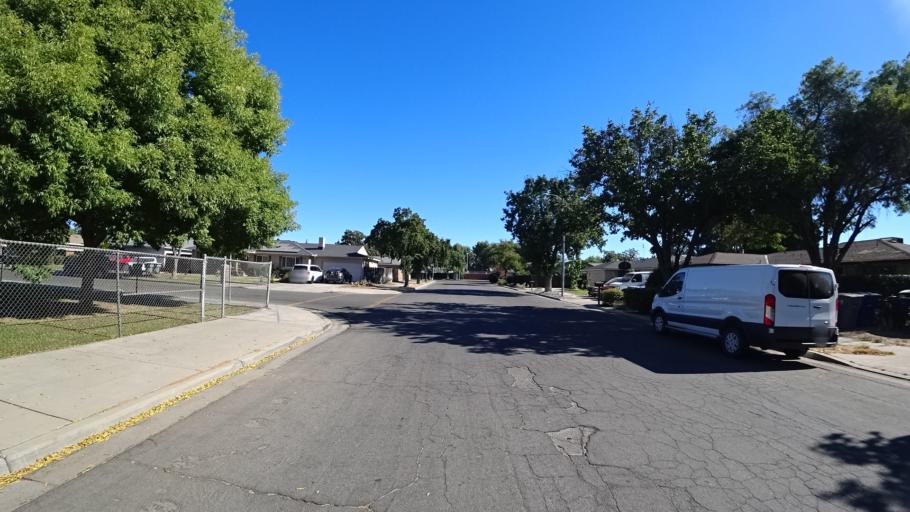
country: US
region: California
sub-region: Fresno County
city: Fresno
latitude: 36.8027
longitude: -119.8399
